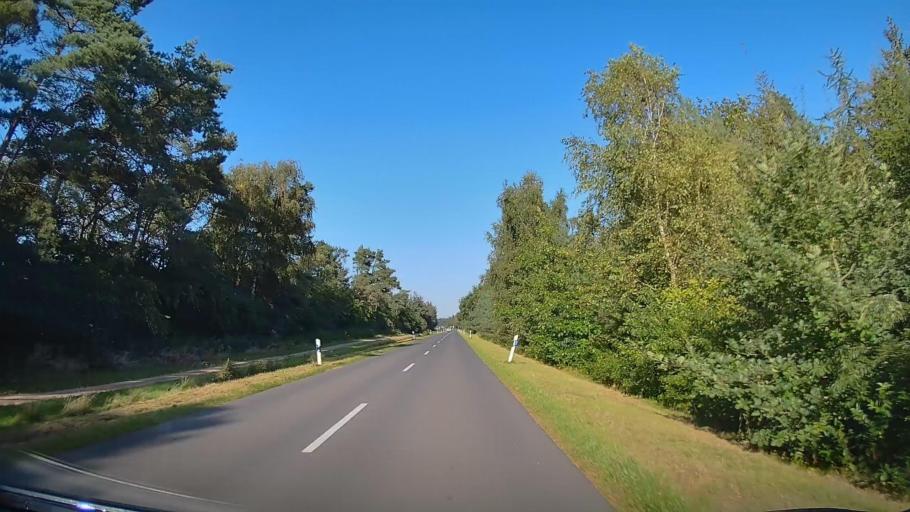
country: DE
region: Lower Saxony
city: Nordholz
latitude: 53.8350
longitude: 8.6151
